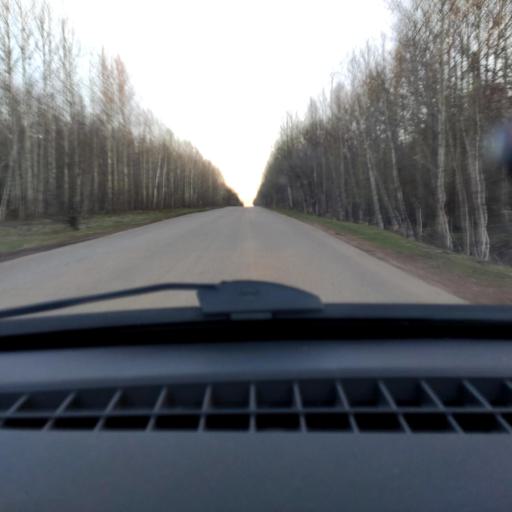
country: RU
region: Bashkortostan
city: Chishmy
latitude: 54.4470
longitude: 55.5521
